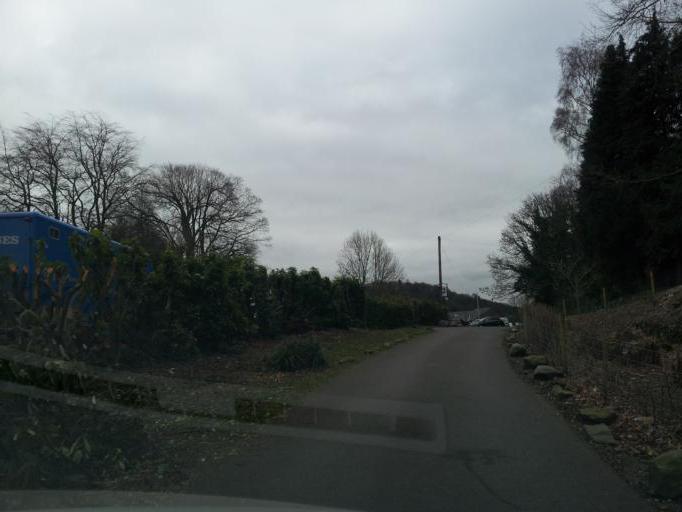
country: GB
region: England
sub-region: Cumbria
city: Windermere
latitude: 54.3686
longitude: -2.9178
